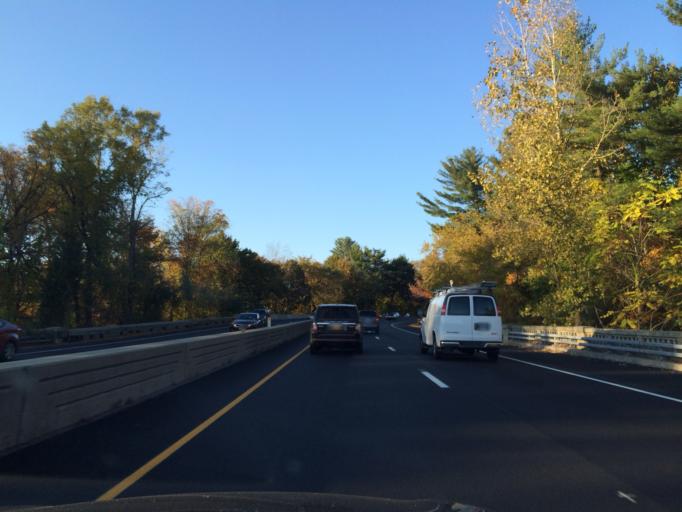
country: US
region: Connecticut
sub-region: Fairfield County
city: Glenville
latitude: 41.0585
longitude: -73.6752
